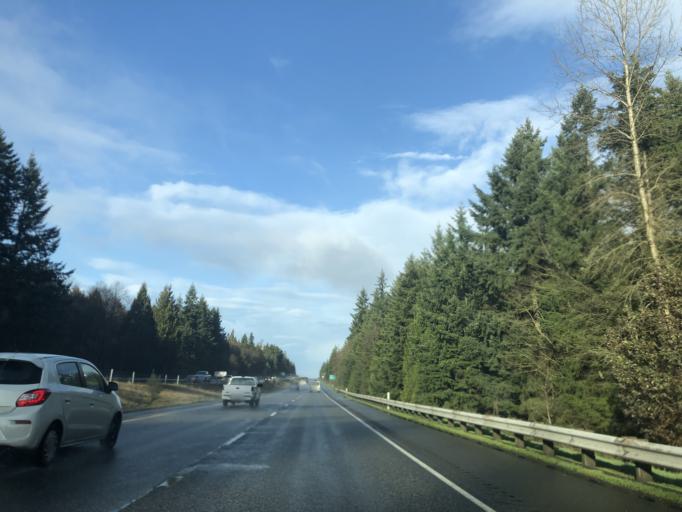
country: US
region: Washington
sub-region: Kitsap County
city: Bangor Trident Base
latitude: 47.7146
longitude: -122.6806
